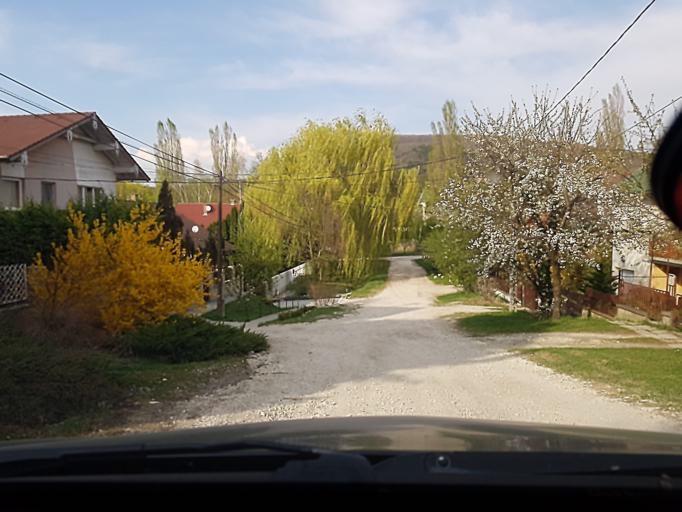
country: HU
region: Pest
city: Piliscsaba
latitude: 47.6378
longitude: 18.8235
